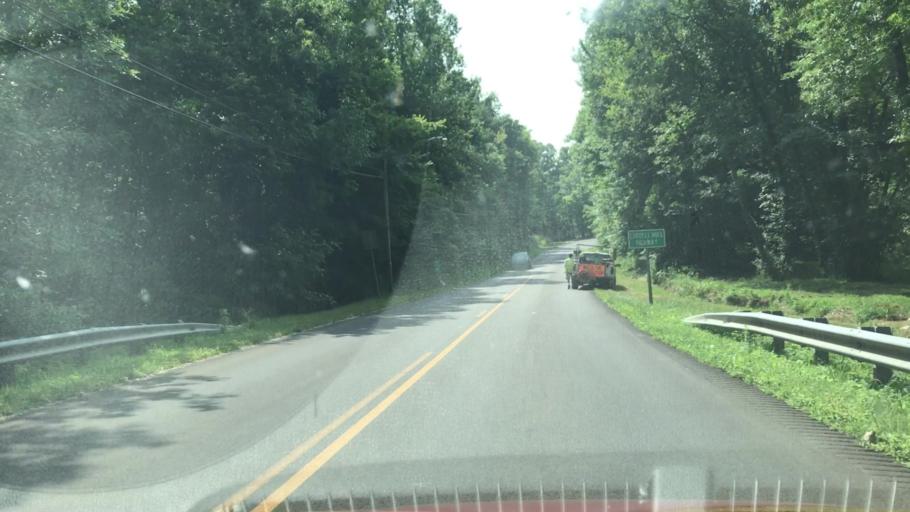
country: US
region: Kentucky
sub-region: Barren County
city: Glasgow
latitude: 36.9877
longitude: -85.9067
